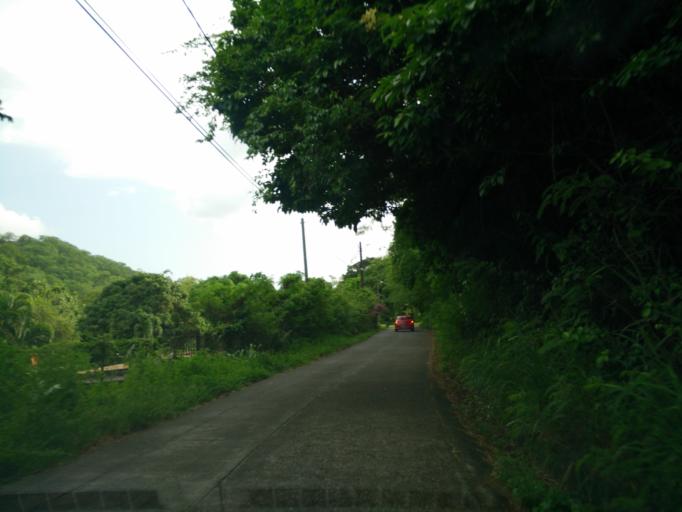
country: MQ
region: Martinique
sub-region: Martinique
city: Saint-Pierre
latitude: 14.7140
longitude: -61.1721
